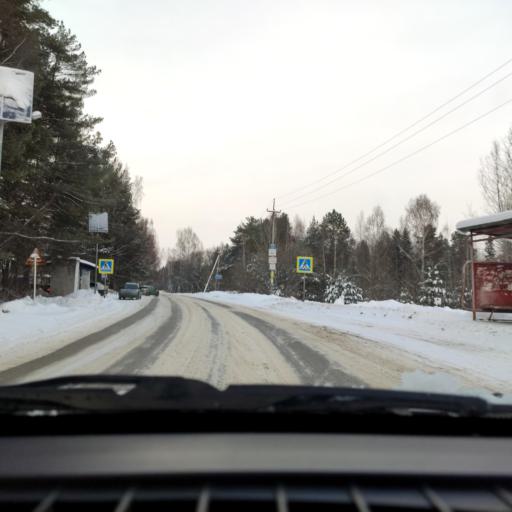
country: RU
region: Perm
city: Overyata
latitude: 58.0481
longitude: 55.8853
